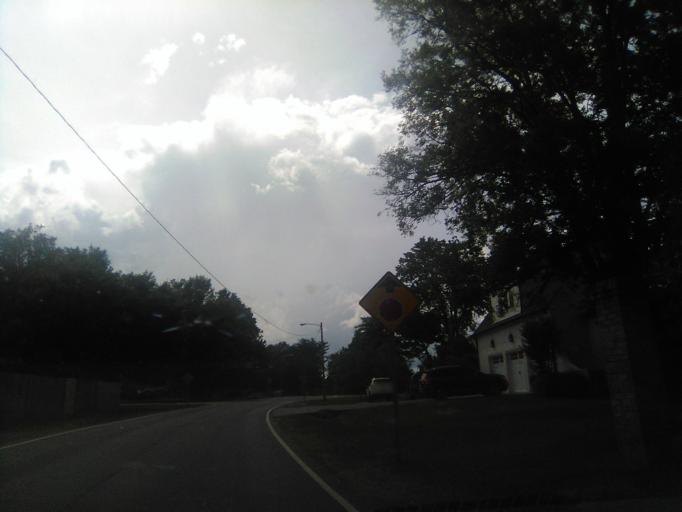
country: US
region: Tennessee
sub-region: Davidson County
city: Belle Meade
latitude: 36.0953
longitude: -86.8685
